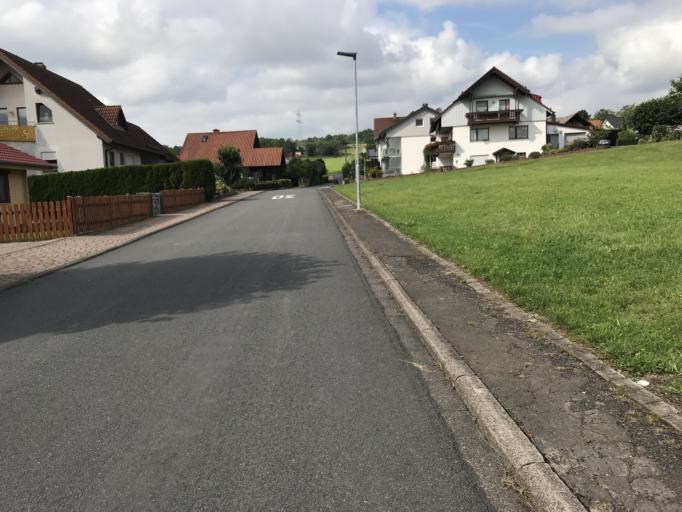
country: DE
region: Hesse
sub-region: Regierungsbezirk Giessen
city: Lauterbach
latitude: 50.6459
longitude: 9.3624
